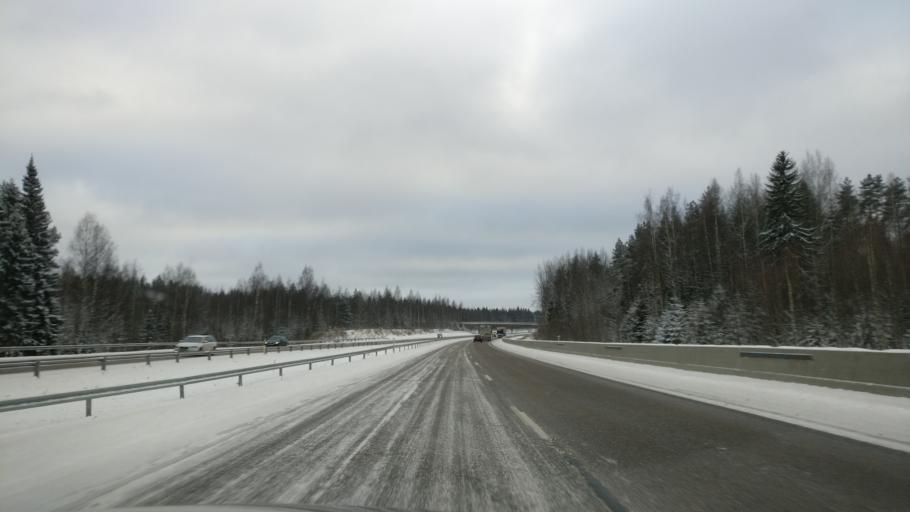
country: FI
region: Paijanne Tavastia
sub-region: Lahti
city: Nastola
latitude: 61.0219
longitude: 25.8296
